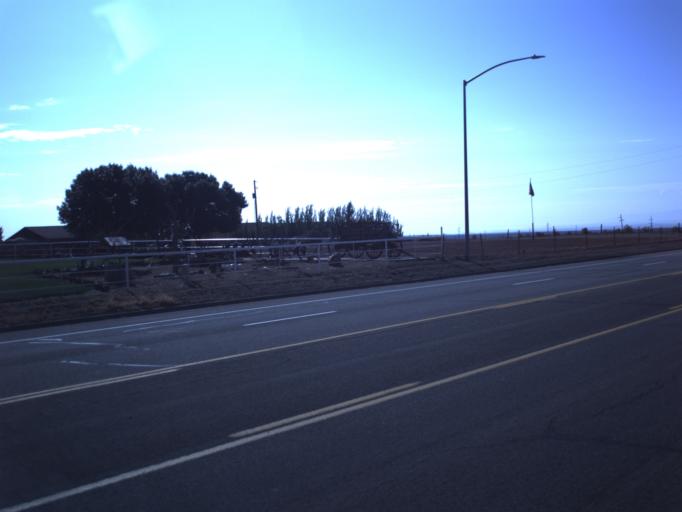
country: US
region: Utah
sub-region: San Juan County
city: Blanding
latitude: 37.6061
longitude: -109.4789
